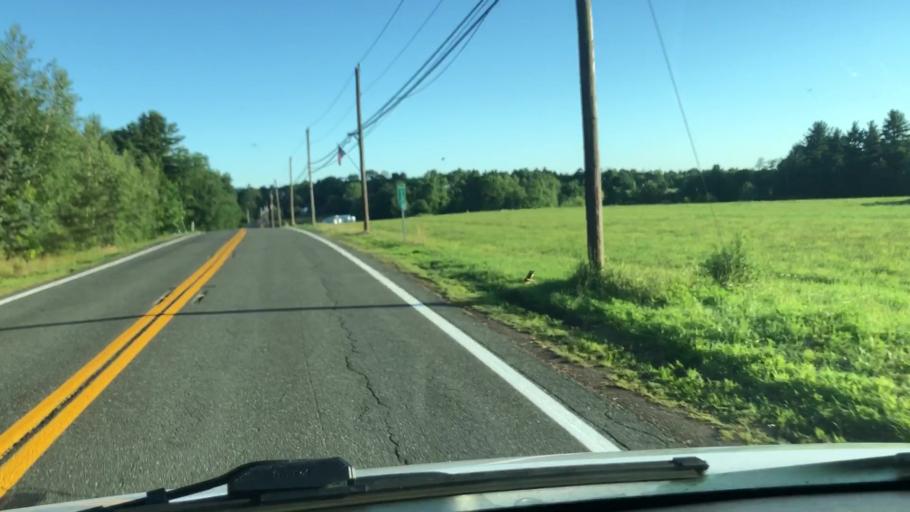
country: US
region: Massachusetts
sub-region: Hampshire County
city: Chesterfield
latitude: 42.3900
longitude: -72.9318
